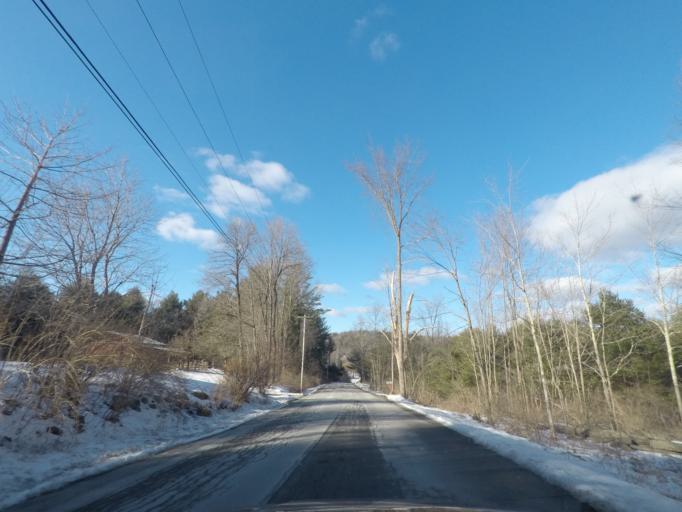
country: US
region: New York
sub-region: Rensselaer County
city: Averill Park
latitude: 42.5524
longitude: -73.5254
